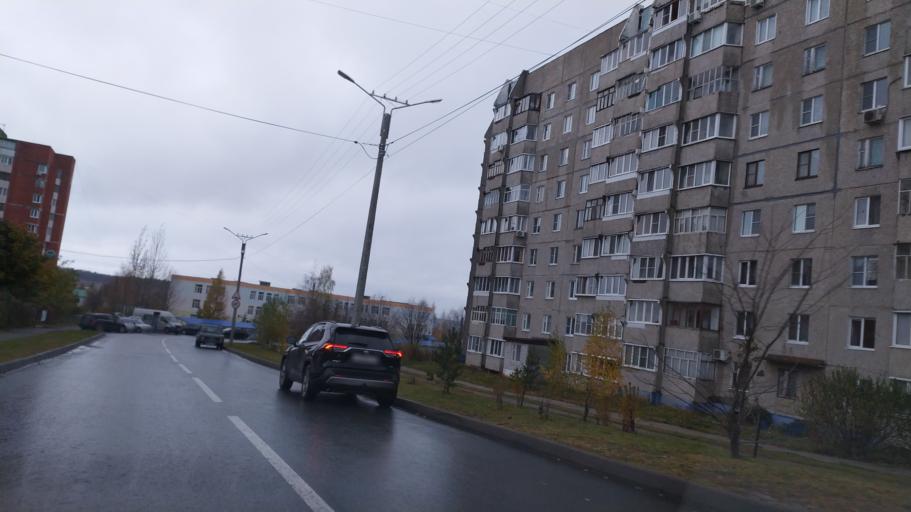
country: RU
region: Chuvashia
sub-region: Cheboksarskiy Rayon
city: Cheboksary
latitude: 56.1431
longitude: 47.1626
